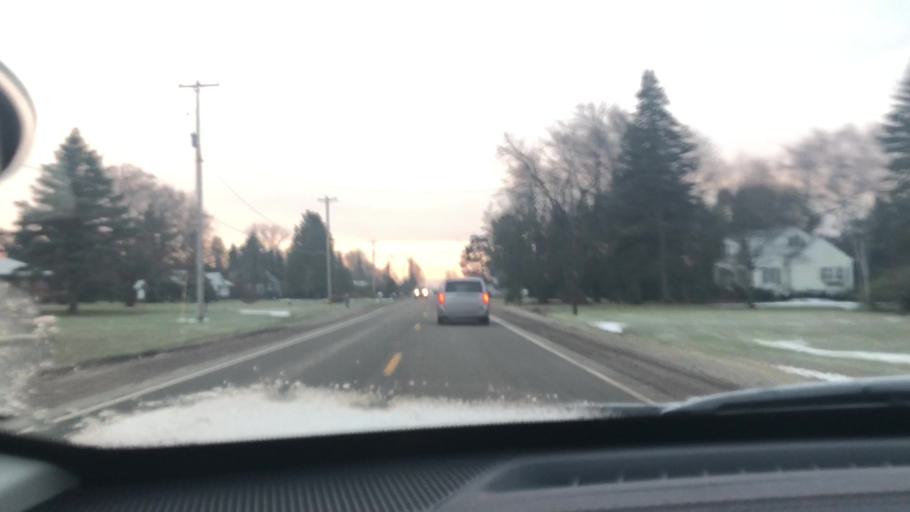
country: US
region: Michigan
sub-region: Saginaw County
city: Buena Vista
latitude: 43.4698
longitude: -83.8374
